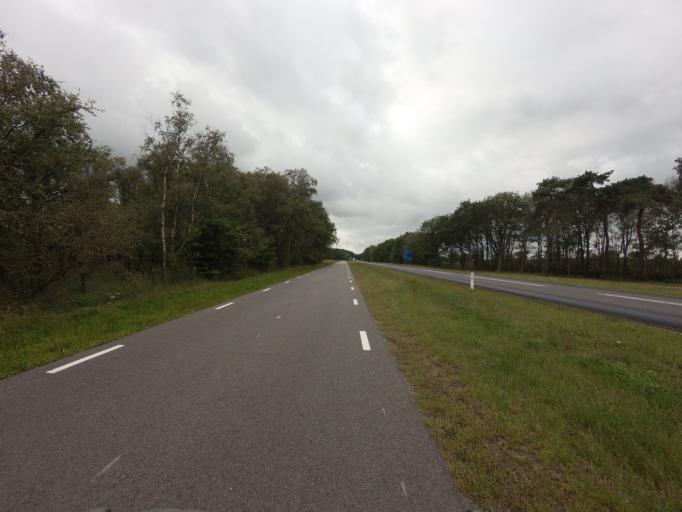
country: NL
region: Friesland
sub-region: Gemeente Heerenveen
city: Jubbega
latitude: 52.9658
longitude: 6.2046
